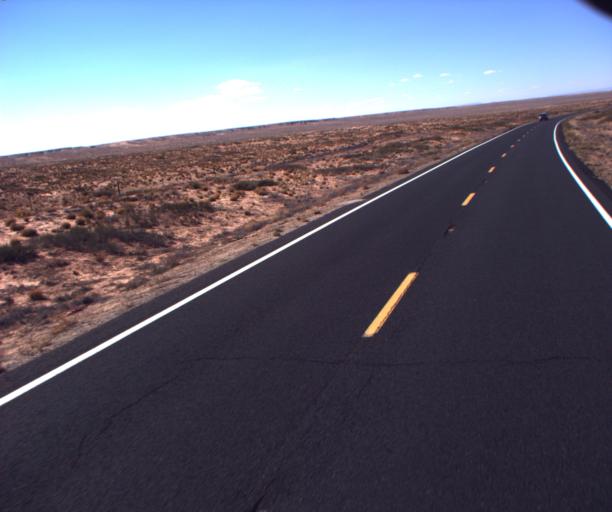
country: US
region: Arizona
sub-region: Coconino County
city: Tuba City
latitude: 36.0204
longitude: -111.1273
